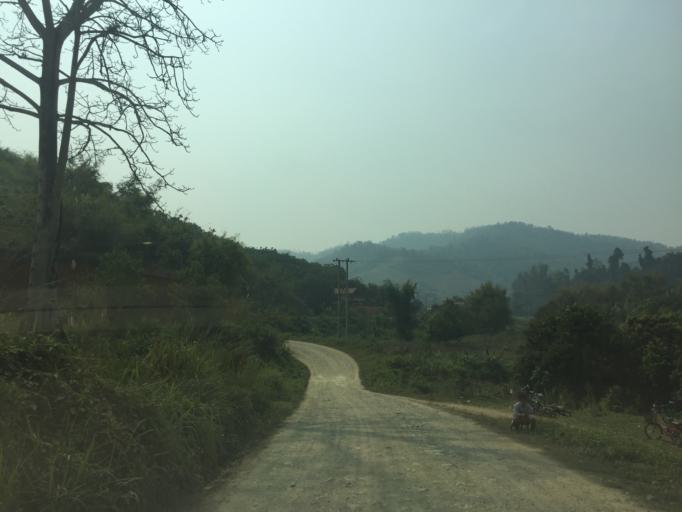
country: TH
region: Phayao
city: Phu Sang
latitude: 19.6151
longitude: 100.5377
